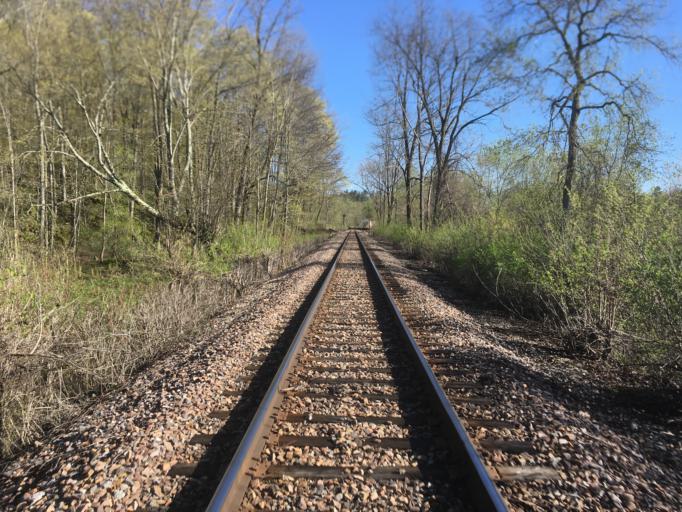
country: US
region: Vermont
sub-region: Rutland County
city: West Rutland
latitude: 43.6480
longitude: -73.0370
